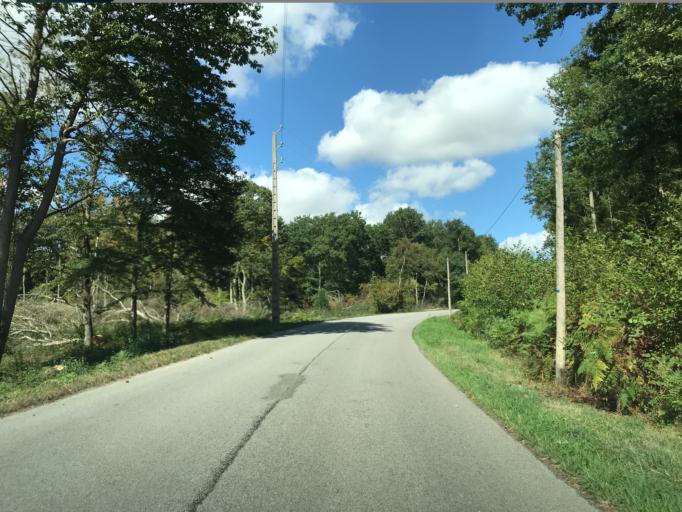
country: FR
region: Haute-Normandie
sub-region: Departement de l'Eure
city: La Chapelle-Reanville
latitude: 49.0909
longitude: 1.3941
